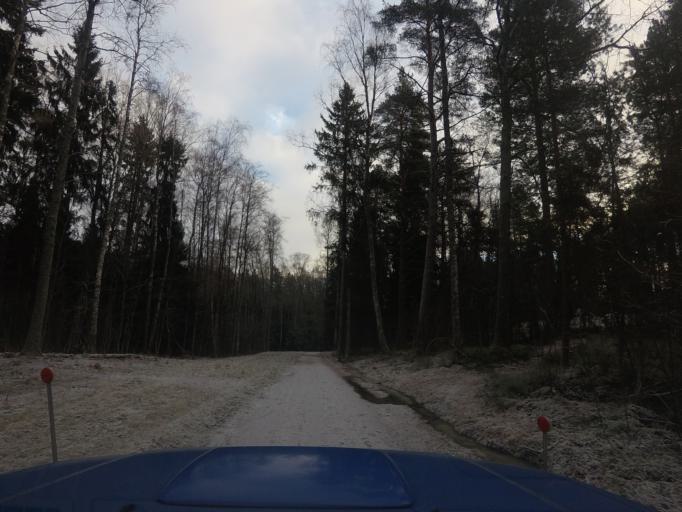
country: FI
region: Uusimaa
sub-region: Helsinki
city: Espoo
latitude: 60.1835
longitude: 24.6583
